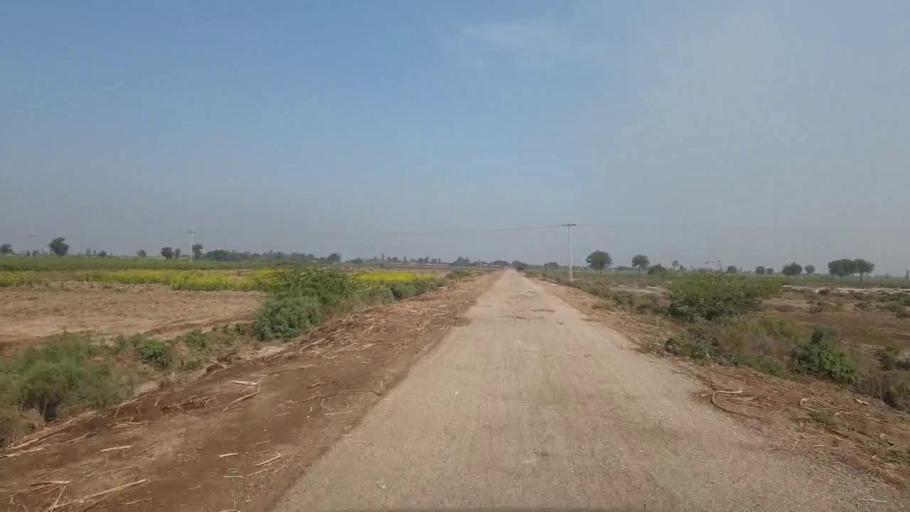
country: PK
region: Sindh
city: Mirwah Gorchani
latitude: 25.3705
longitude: 69.1611
